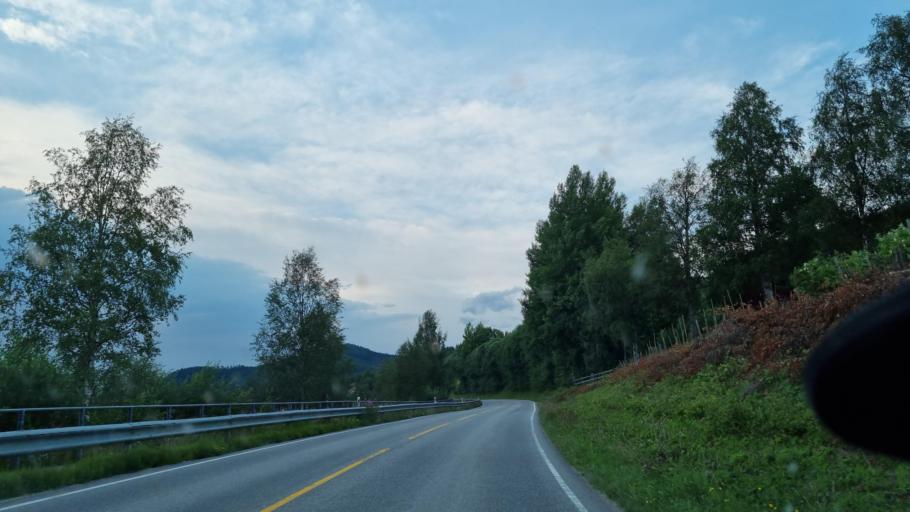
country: NO
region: Hedmark
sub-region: Trysil
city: Innbygda
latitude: 61.3060
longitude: 12.2729
